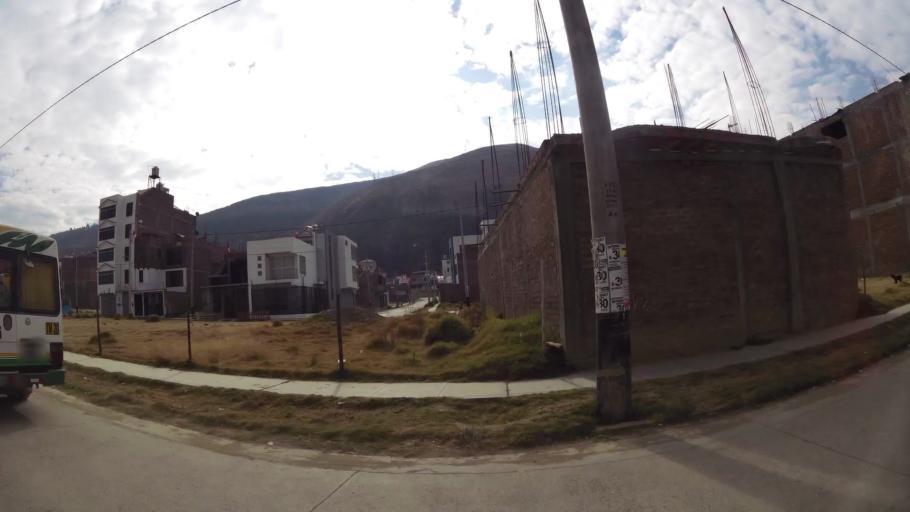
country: PE
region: Junin
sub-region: Provincia de Huancayo
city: Huancayo
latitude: -12.0503
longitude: -75.1886
